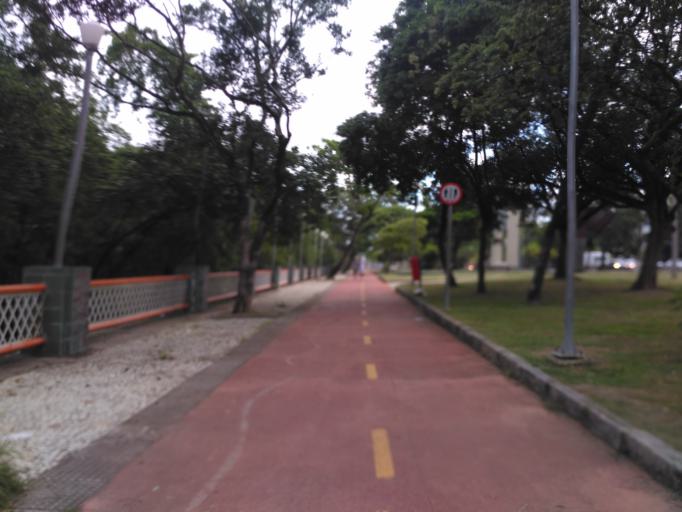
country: BR
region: Pernambuco
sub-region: Recife
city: Recife
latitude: -8.0560
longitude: -34.8773
